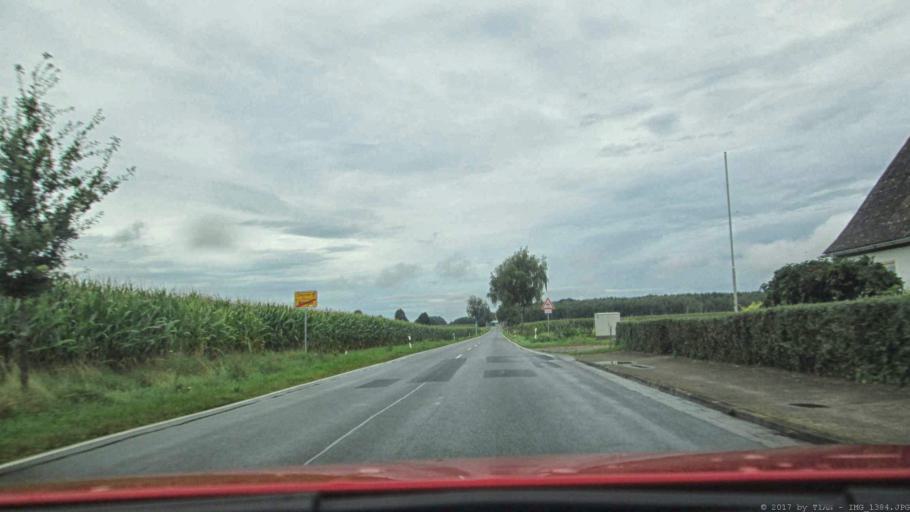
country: DE
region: Lower Saxony
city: Wittingen
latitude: 52.7363
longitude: 10.7365
